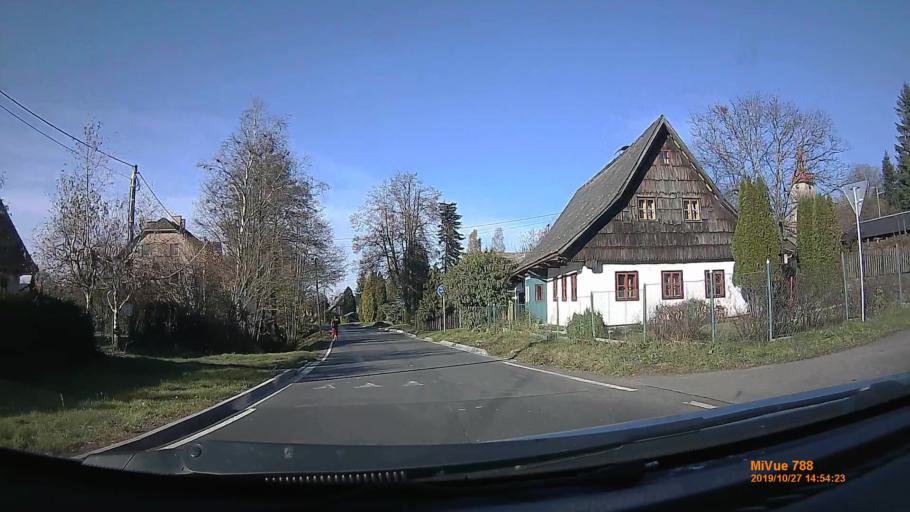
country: CZ
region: Pardubicky
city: Cervena Voda
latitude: 50.0766
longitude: 16.7107
